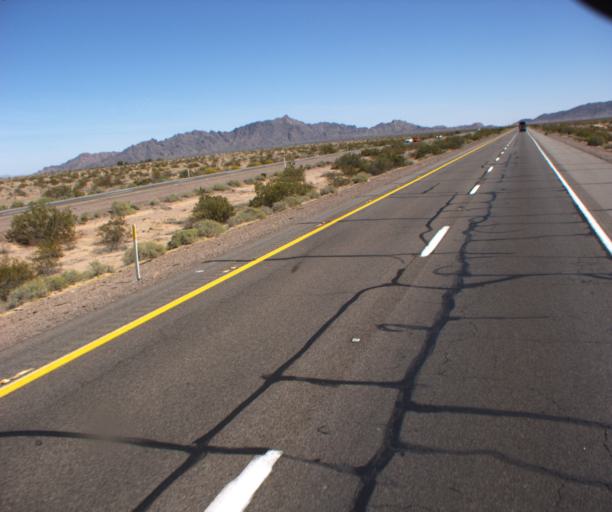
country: US
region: Arizona
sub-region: Yuma County
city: Wellton
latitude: 32.7103
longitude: -113.8415
